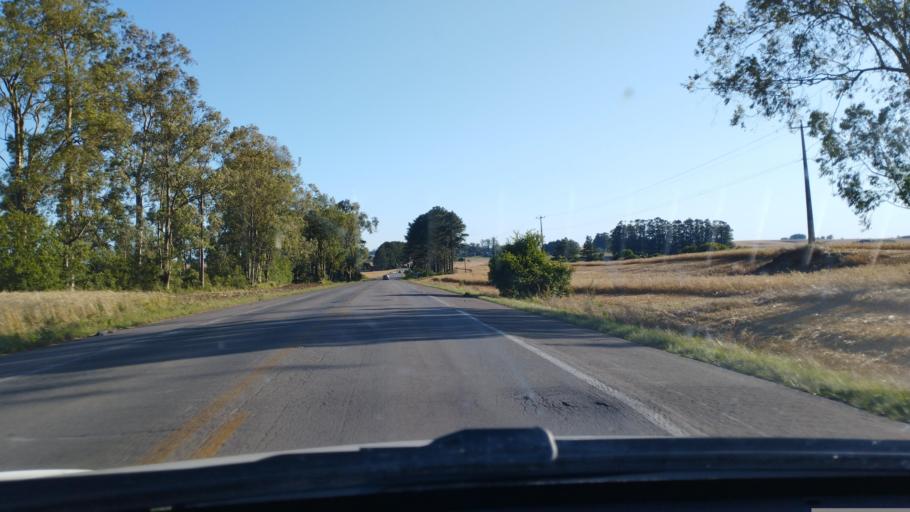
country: BR
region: Rio Grande do Sul
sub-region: Julio De Castilhos
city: Julio de Castilhos
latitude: -29.4288
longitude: -53.6746
